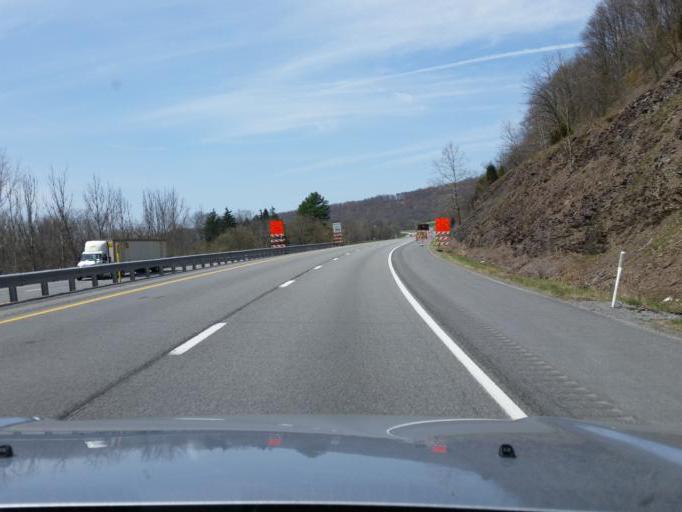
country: US
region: Pennsylvania
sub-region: Perry County
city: Newport
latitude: 40.5648
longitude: -77.1929
